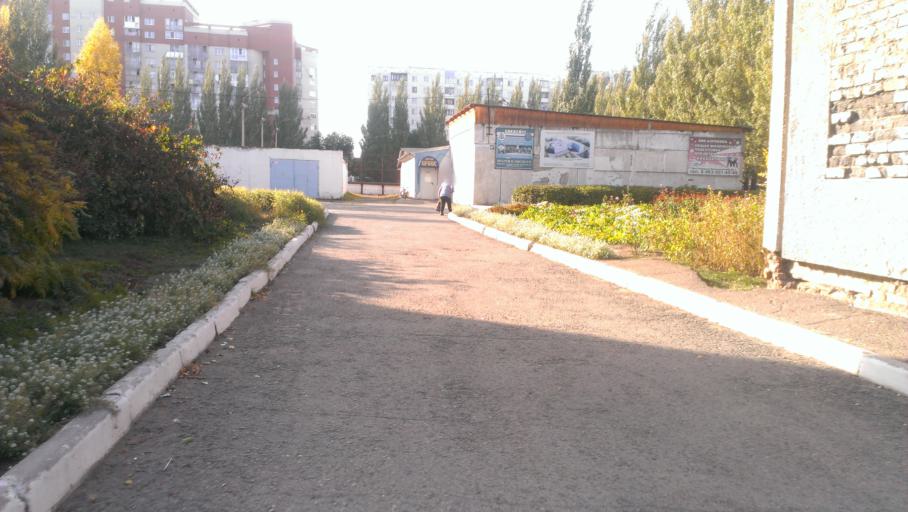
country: RU
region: Altai Krai
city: Novosilikatnyy
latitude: 53.3336
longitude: 83.6723
